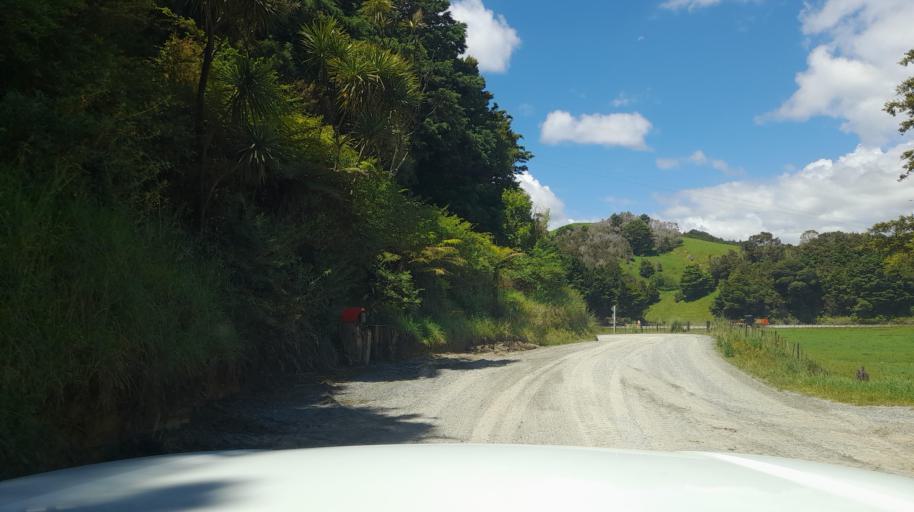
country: NZ
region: Northland
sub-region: Far North District
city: Kaitaia
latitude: -35.1080
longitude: 173.3933
